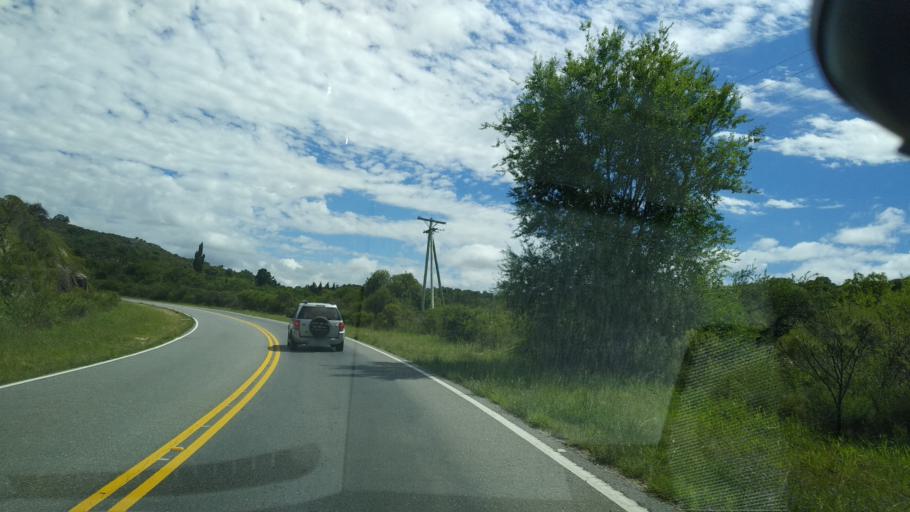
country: AR
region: Cordoba
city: Mina Clavero
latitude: -31.7591
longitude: -64.9588
